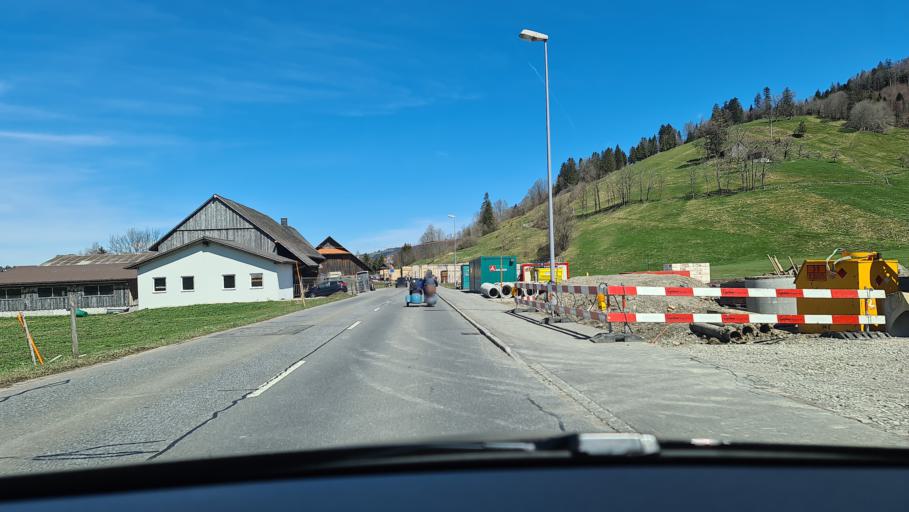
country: CH
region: Schwyz
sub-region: Bezirk Einsiedeln
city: Einsiedeln
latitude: 47.1185
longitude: 8.7397
